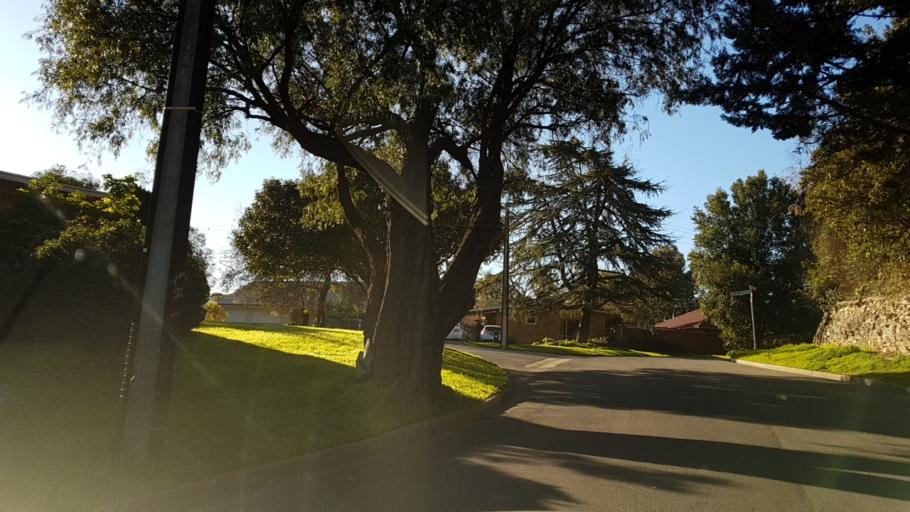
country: AU
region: South Australia
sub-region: Campbelltown
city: Hectorville
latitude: -34.8838
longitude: 138.6571
